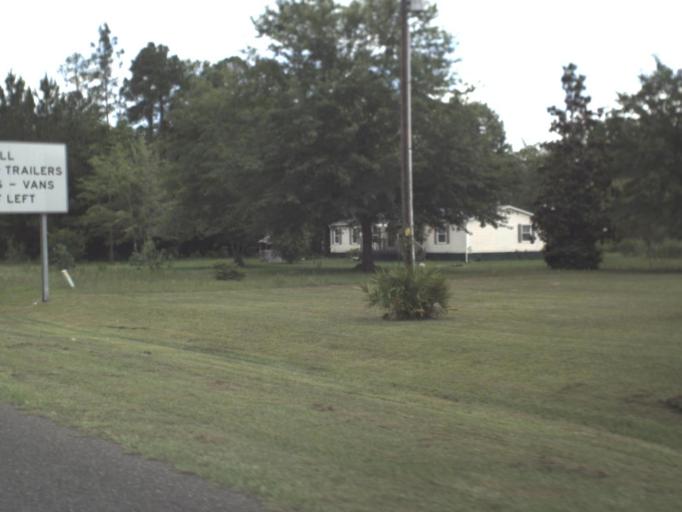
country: US
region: Florida
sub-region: Nassau County
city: Hilliard
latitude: 30.7340
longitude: -81.9476
